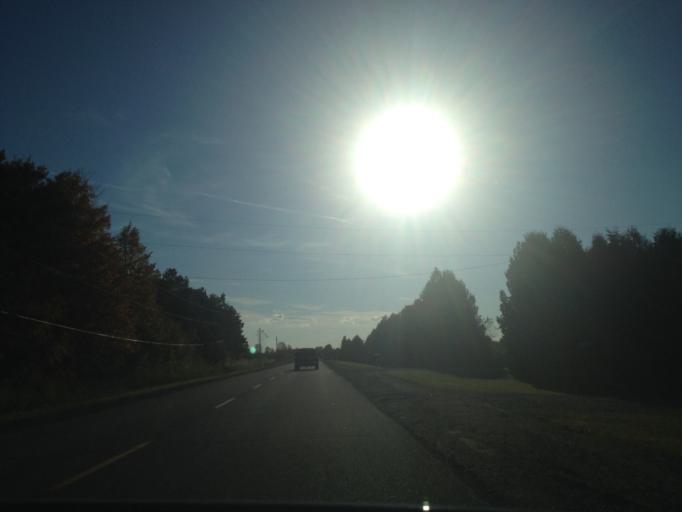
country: CA
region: Ontario
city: Delaware
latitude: 42.6180
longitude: -81.5857
